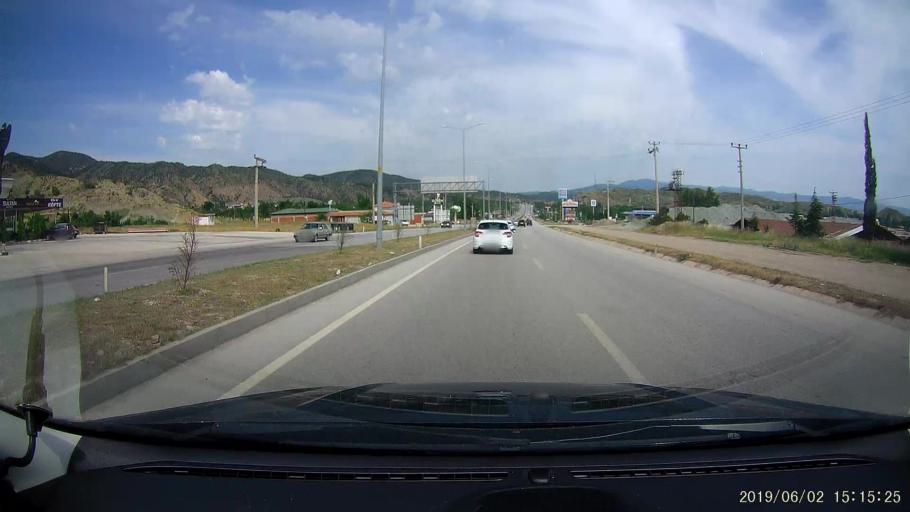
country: TR
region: Corum
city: Osmancik
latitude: 40.9709
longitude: 34.8486
